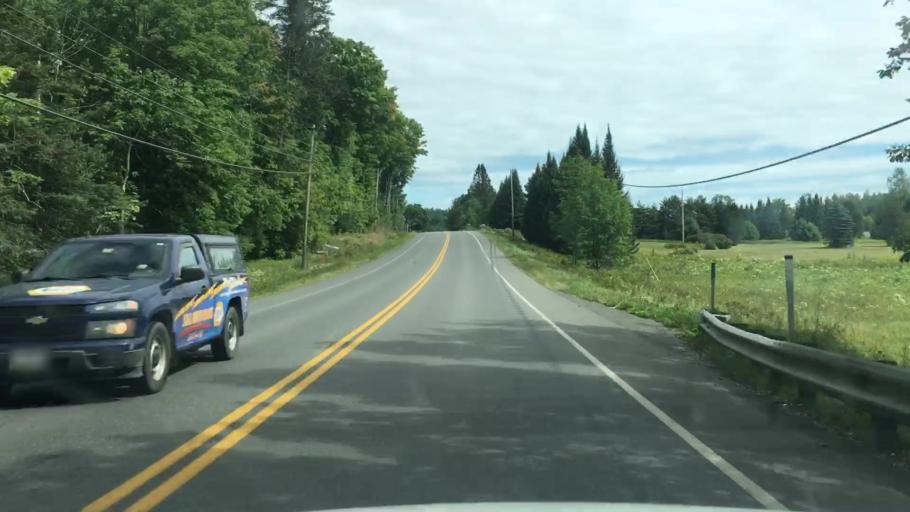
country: US
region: Maine
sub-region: Piscataquis County
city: Dover-Foxcroft
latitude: 45.2031
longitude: -69.1867
